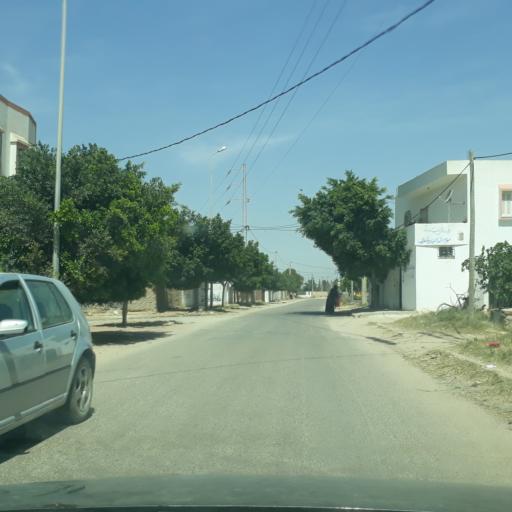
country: TN
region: Safaqis
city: Al Qarmadah
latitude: 34.8276
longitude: 10.7825
